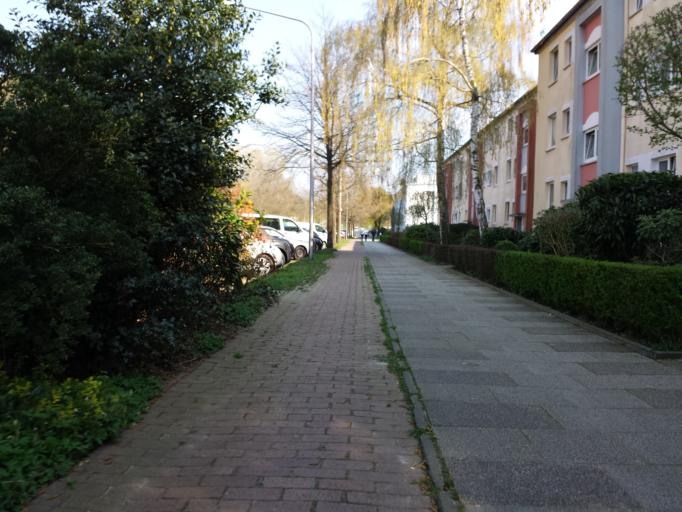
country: DE
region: Lower Saxony
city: Lilienthal
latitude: 53.0861
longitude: 8.8930
